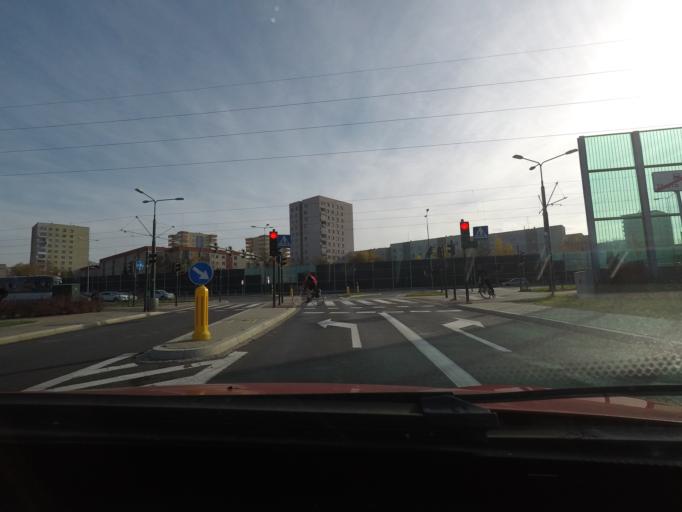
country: PL
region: Lesser Poland Voivodeship
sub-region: Krakow
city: Krakow
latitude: 50.0273
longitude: 19.9053
